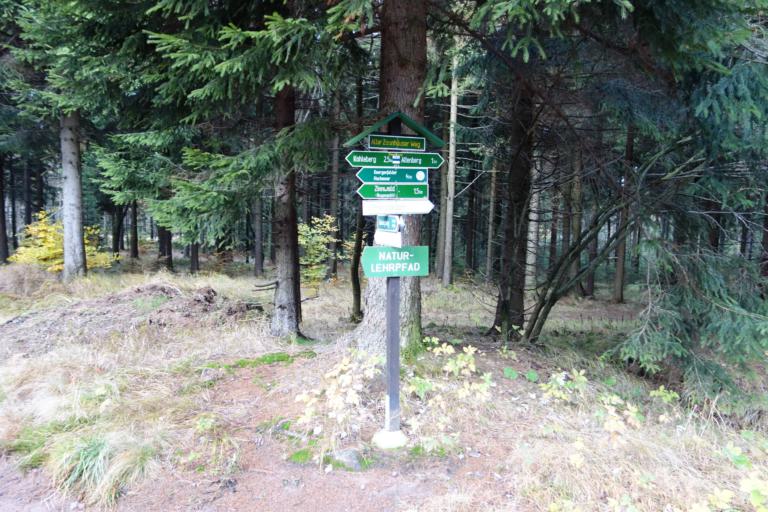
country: DE
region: Saxony
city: Altenberg
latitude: 50.7574
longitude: 13.7510
